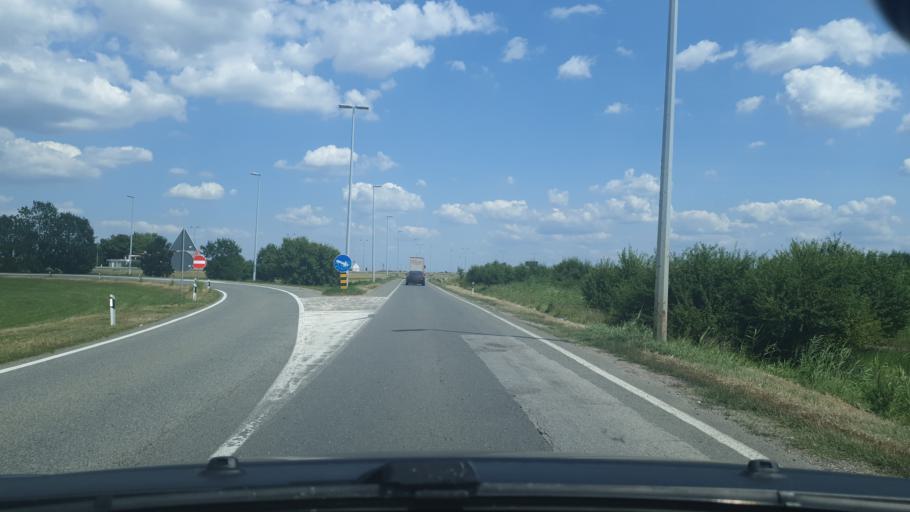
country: RS
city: Simanovci
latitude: 44.8754
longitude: 20.1239
